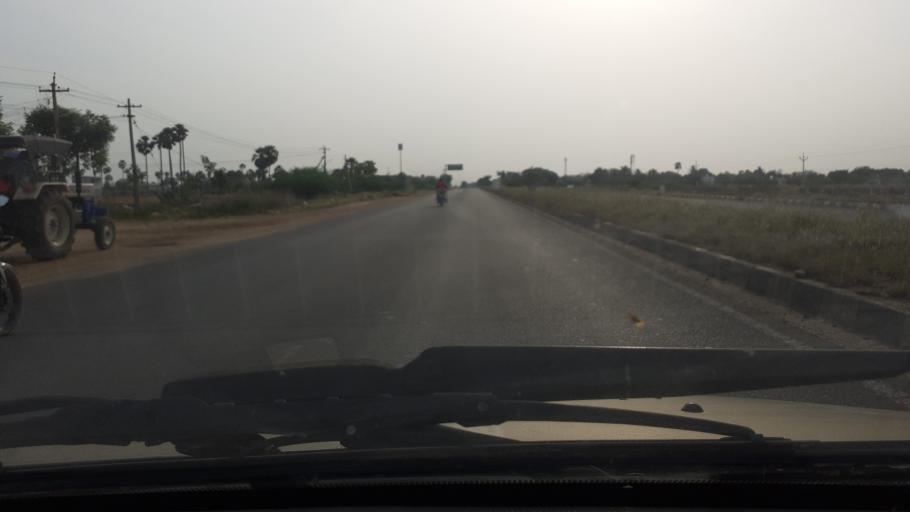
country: IN
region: Tamil Nadu
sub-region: Thoothukkudi
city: Korampallam
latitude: 8.7345
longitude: 78.0067
